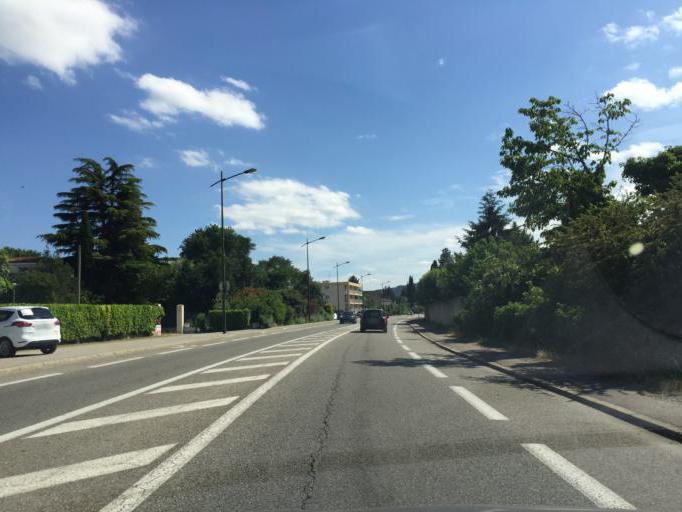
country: FR
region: Rhone-Alpes
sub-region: Departement de l'Ardeche
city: Tournon-sur-Rhone
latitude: 45.0607
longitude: 4.8419
